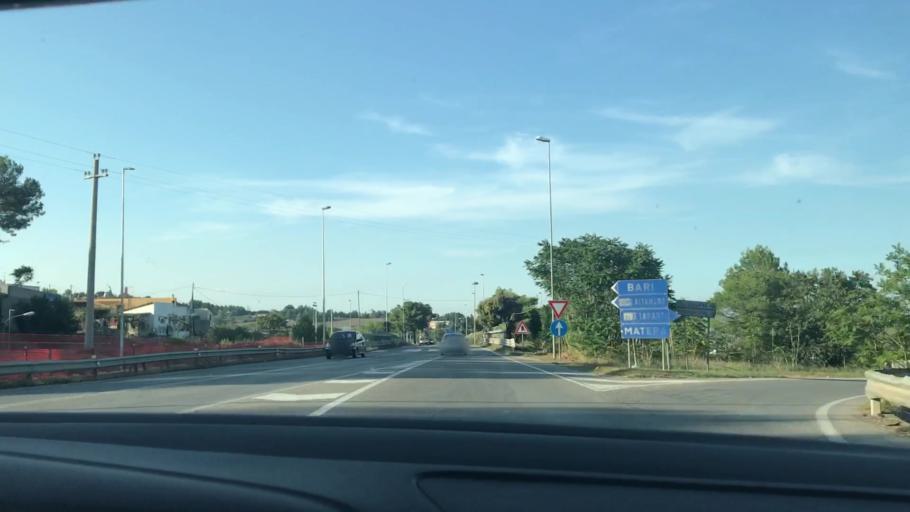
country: IT
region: Basilicate
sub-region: Provincia di Matera
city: Matera
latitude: 40.6836
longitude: 16.5902
